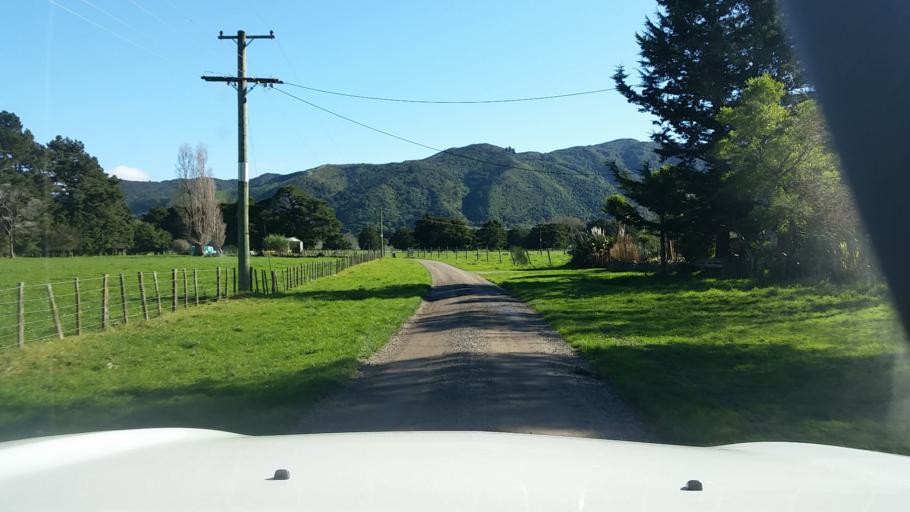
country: NZ
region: Wellington
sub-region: Masterton District
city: Masterton
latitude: -41.0562
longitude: 175.4099
